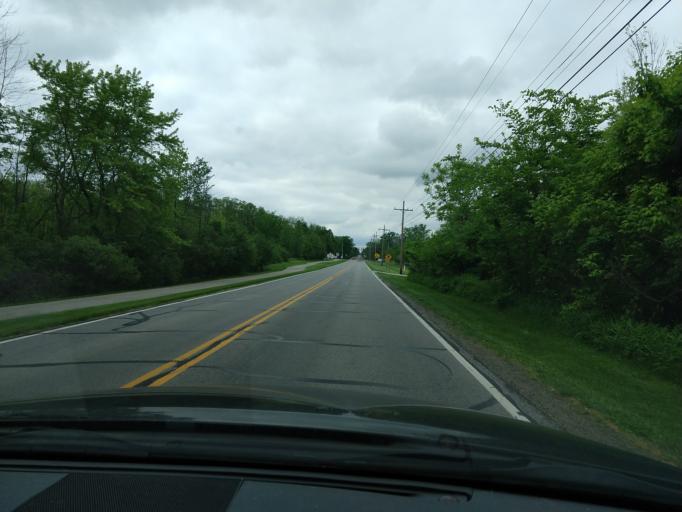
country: US
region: Indiana
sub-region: Hamilton County
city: Westfield
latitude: 40.0197
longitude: -86.1275
